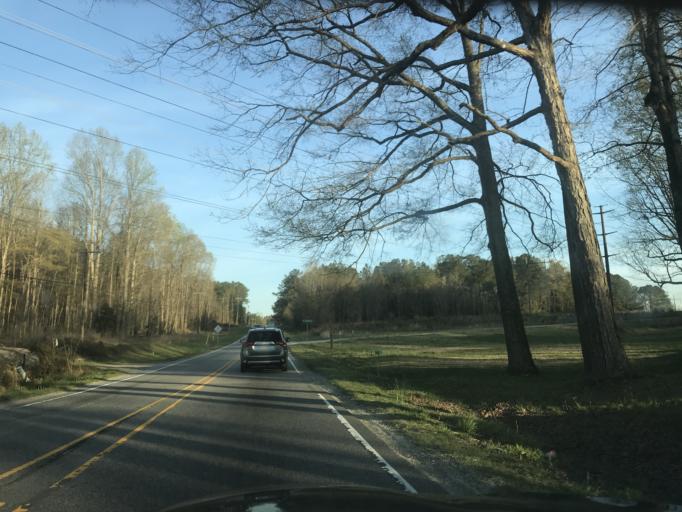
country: US
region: North Carolina
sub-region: Wake County
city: Garner
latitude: 35.7374
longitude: -78.5662
